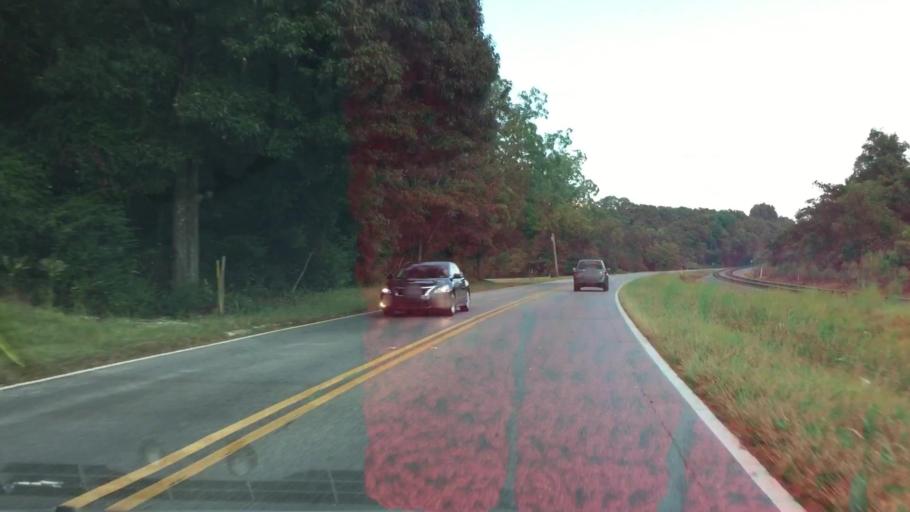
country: US
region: Georgia
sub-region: Clayton County
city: Lovejoy
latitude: 33.4320
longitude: -84.2929
